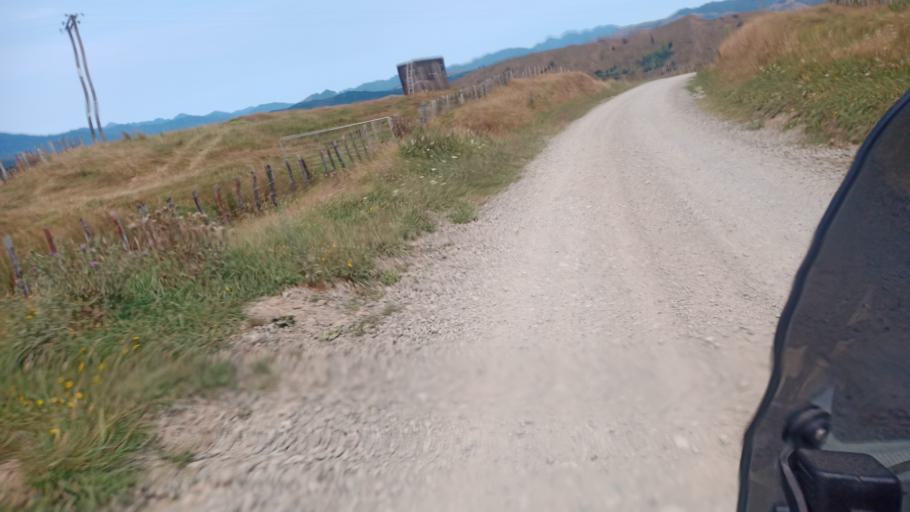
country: NZ
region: Bay of Plenty
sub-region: Opotiki District
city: Opotiki
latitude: -37.6571
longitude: 178.1226
